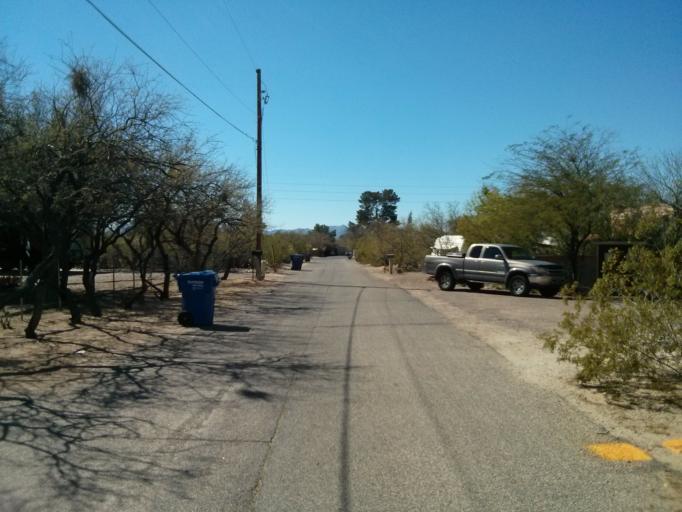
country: US
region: Arizona
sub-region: Pima County
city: Catalina Foothills
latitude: 32.2740
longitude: -110.9509
